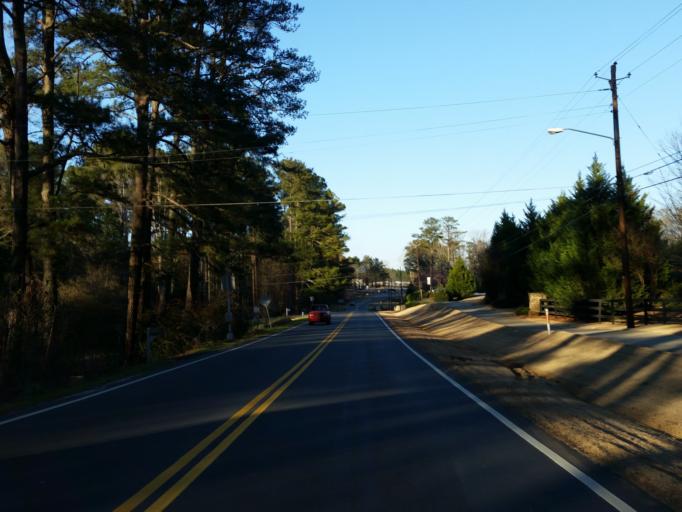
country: US
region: Georgia
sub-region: Cherokee County
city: Woodstock
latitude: 34.1113
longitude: -84.5170
